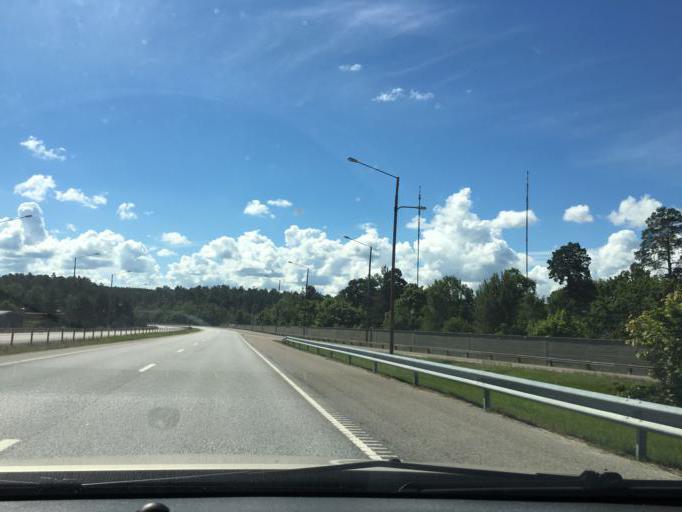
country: SE
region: Stockholm
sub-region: Nacka Kommun
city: Nacka
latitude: 59.3082
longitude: 18.1807
